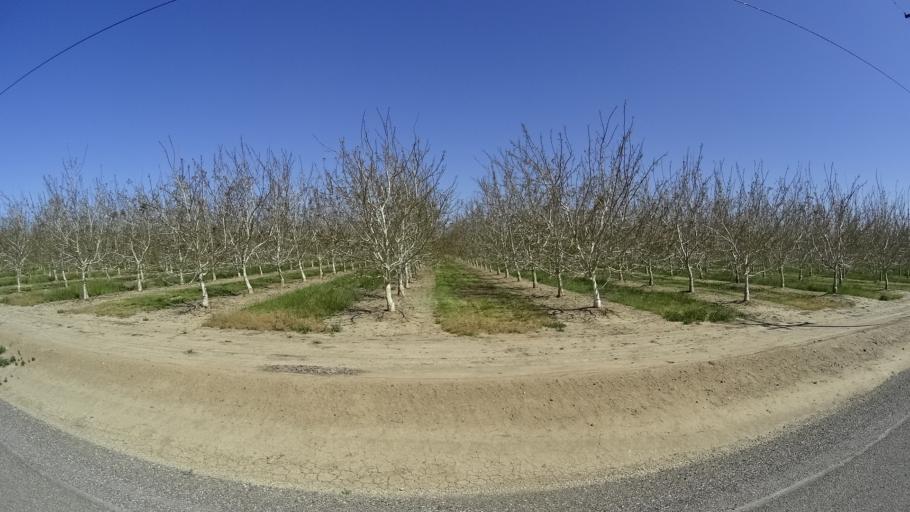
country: US
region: California
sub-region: Glenn County
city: Orland
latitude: 39.7105
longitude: -122.1162
